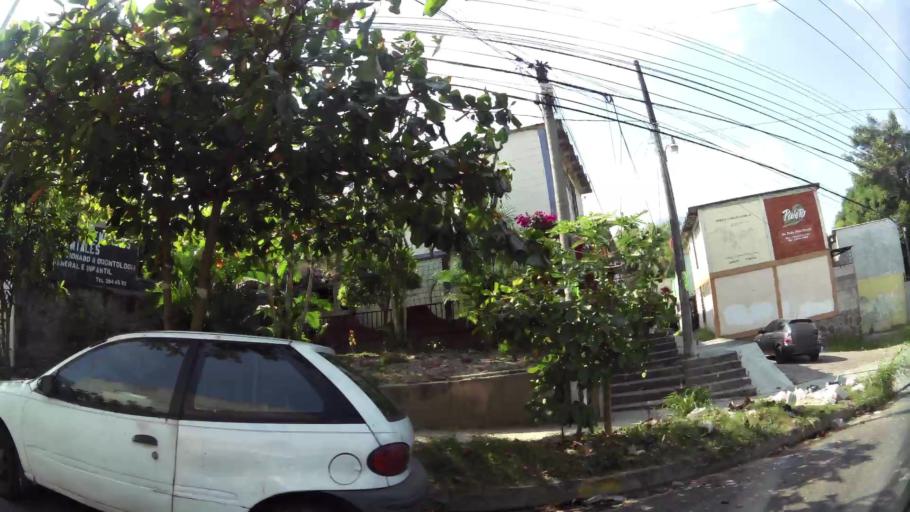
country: SV
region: San Salvador
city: Mejicanos
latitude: 13.7241
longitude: -89.2114
